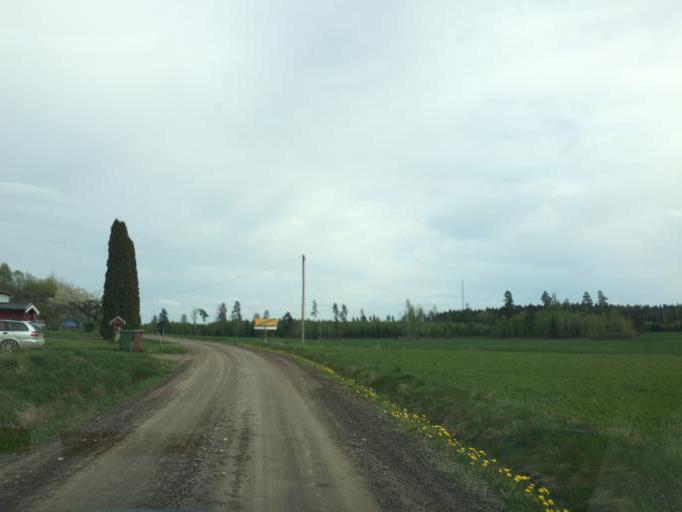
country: SE
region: Vaestmanland
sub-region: Kopings Kommun
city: Koping
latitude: 59.6163
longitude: 16.0408
